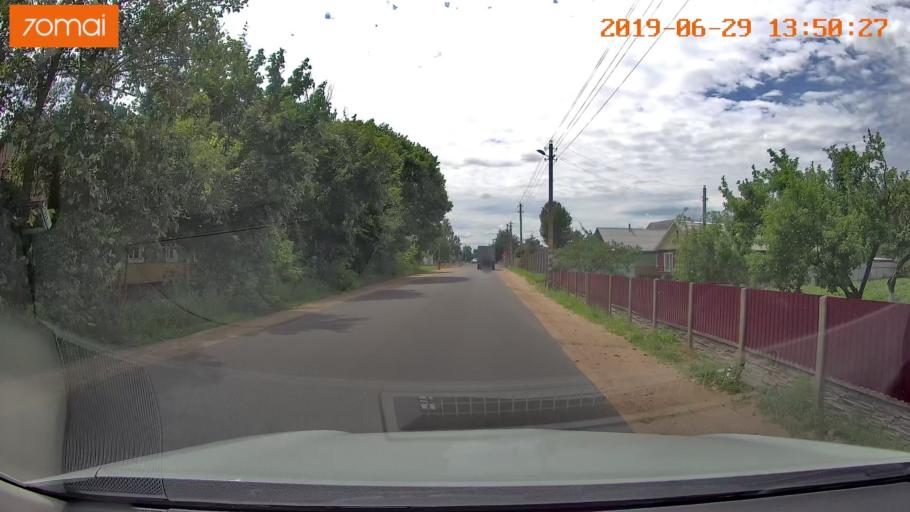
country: BY
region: Minsk
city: Slutsk
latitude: 53.0028
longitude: 27.5667
